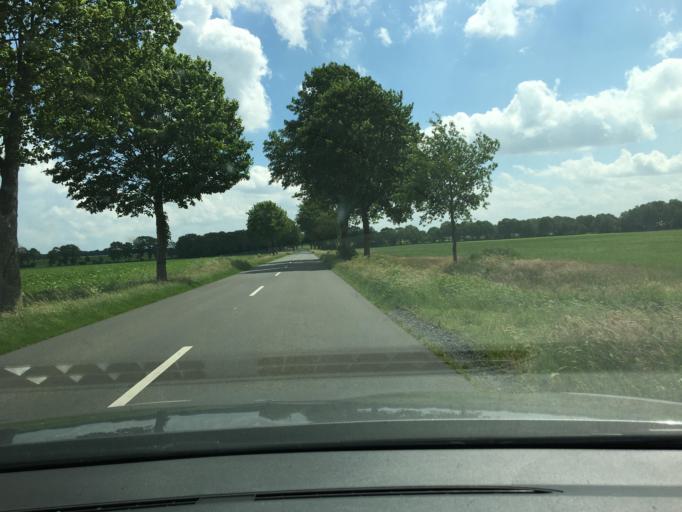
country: DE
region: Lower Saxony
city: Tarmstedt
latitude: 53.2343
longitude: 9.0544
